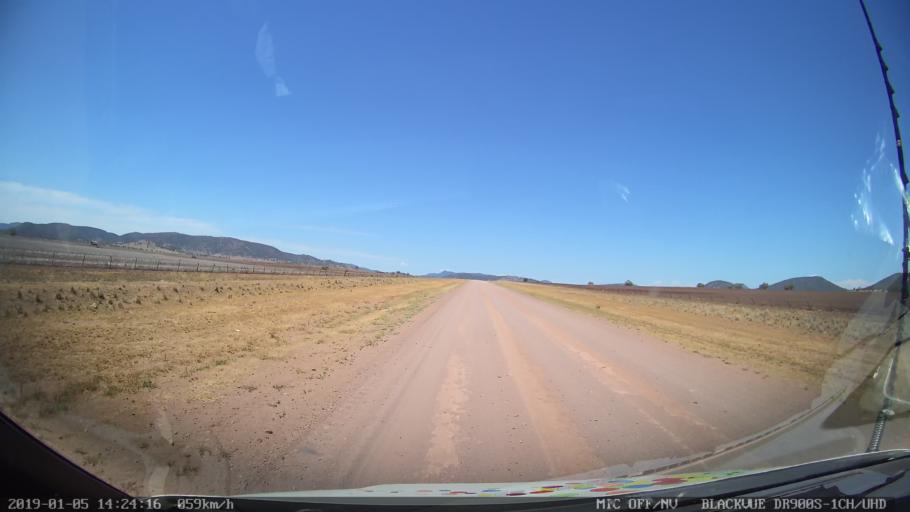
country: AU
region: New South Wales
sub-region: Liverpool Plains
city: Quirindi
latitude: -31.2416
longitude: 150.5382
